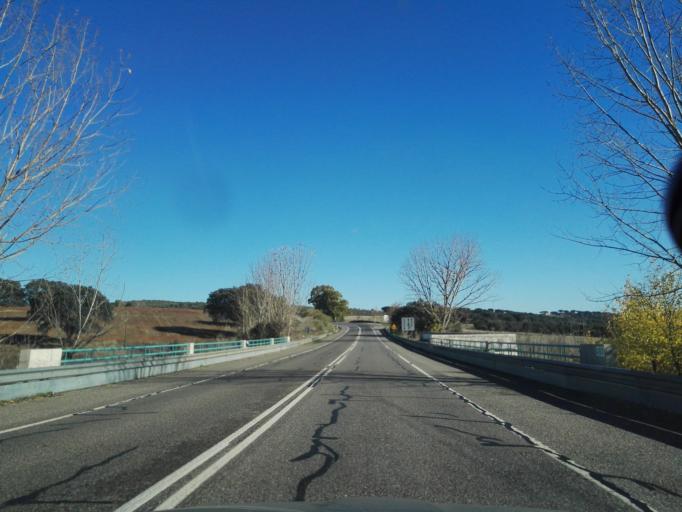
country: PT
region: Evora
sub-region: Vila Vicosa
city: Vila Vicosa
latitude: 38.8414
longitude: -7.3907
